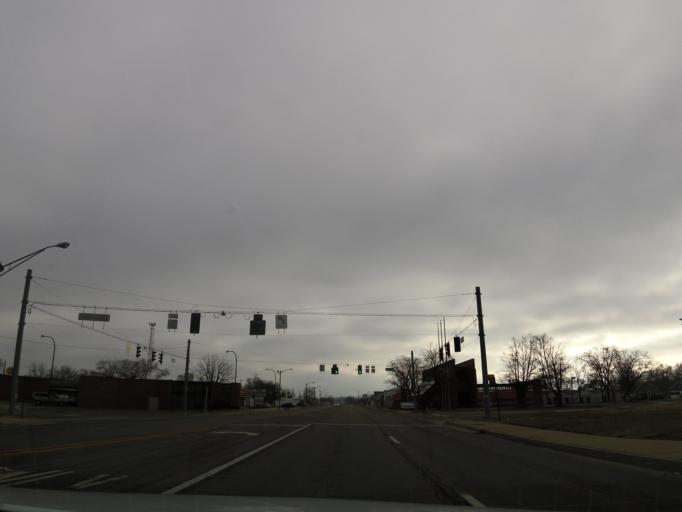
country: US
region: Indiana
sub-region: Bartholomew County
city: Columbus
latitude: 39.1966
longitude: -85.9019
